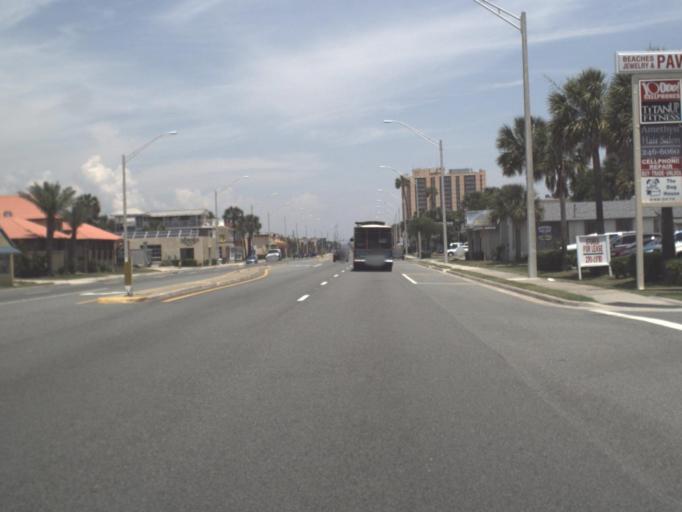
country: US
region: Florida
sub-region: Duval County
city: Jacksonville Beach
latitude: 30.2815
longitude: -81.3903
